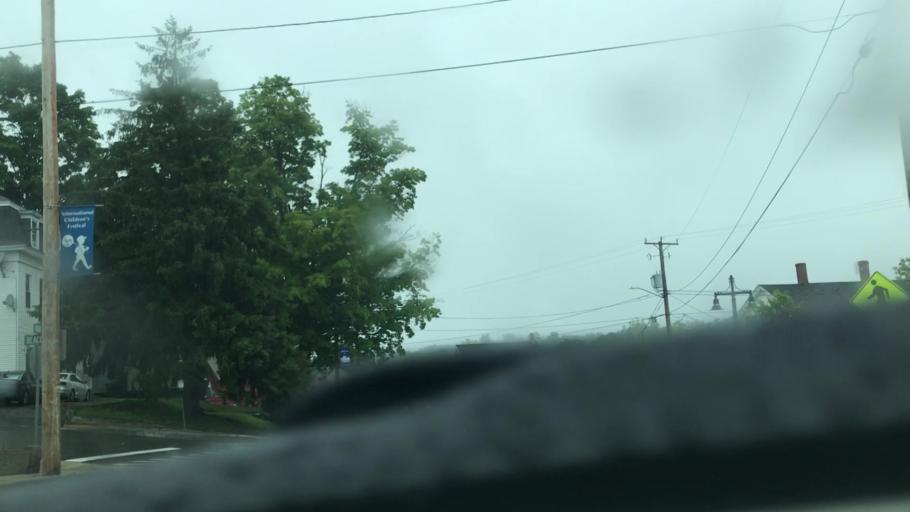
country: US
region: New Hampshire
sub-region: Strafford County
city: Somersworth
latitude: 43.2633
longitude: -70.8642
